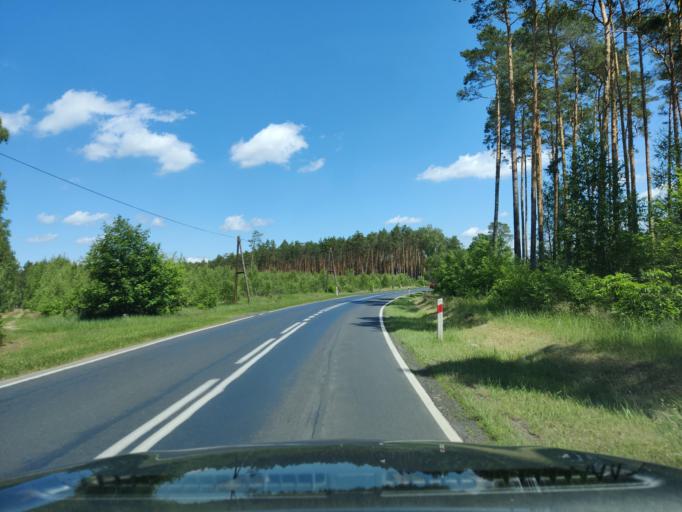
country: PL
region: Greater Poland Voivodeship
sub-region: Powiat nowotomyski
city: Nowy Tomysl
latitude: 52.2290
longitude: 16.1088
